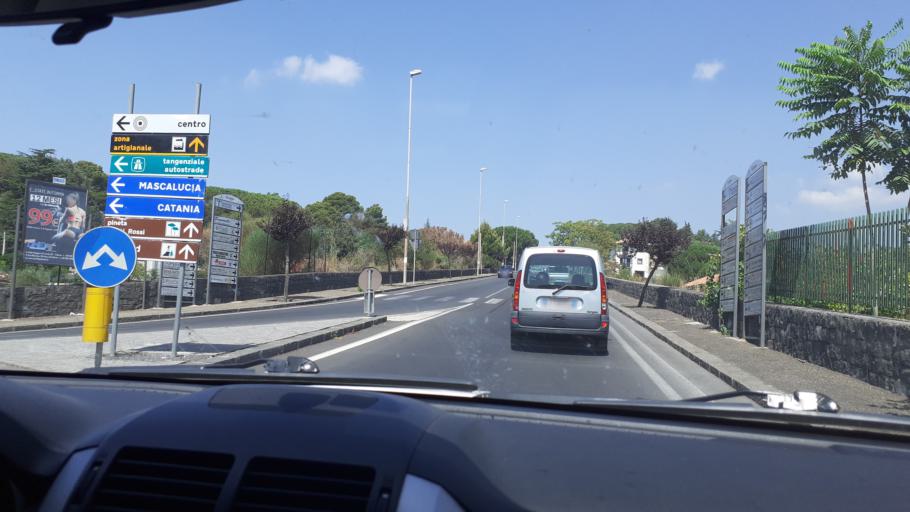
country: IT
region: Sicily
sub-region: Catania
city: Nicolosi
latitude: 37.6147
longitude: 15.0363
